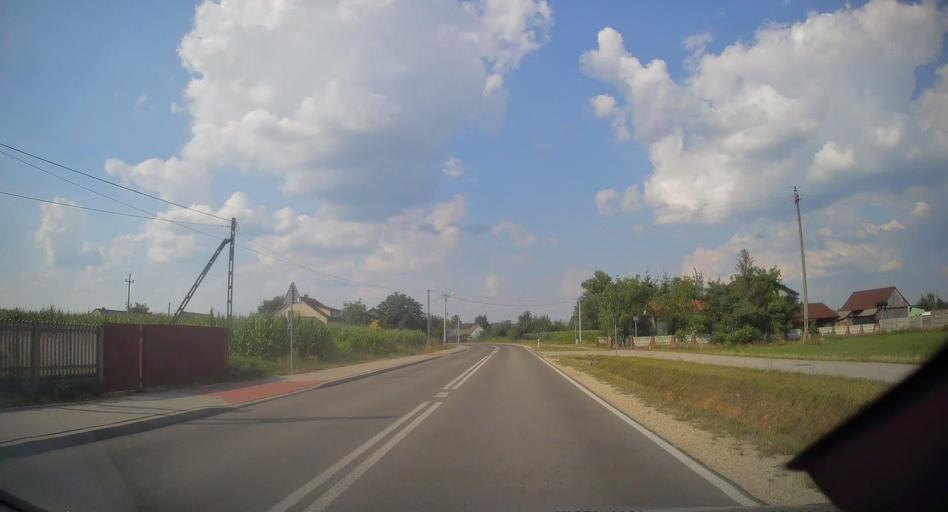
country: PL
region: Swietokrzyskie
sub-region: Powiat konecki
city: Radoszyce
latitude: 51.0452
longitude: 20.2836
